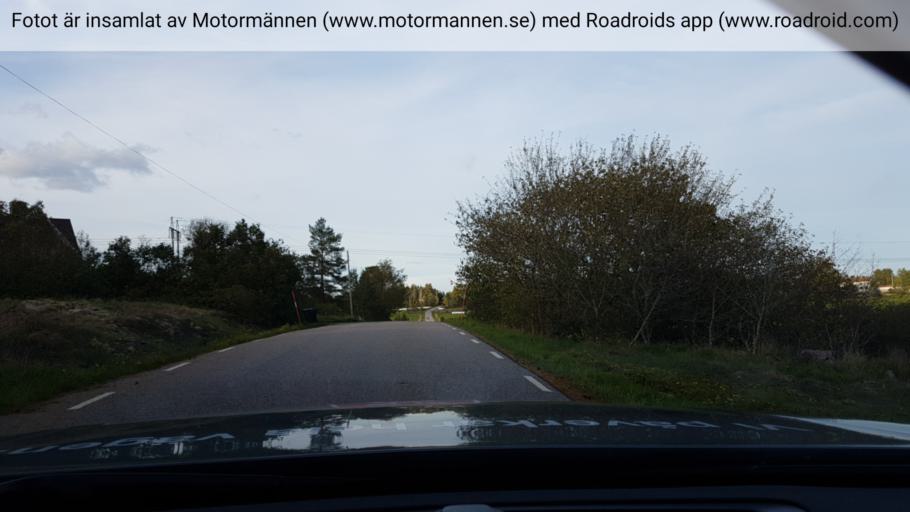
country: SE
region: Kalmar
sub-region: Vasterviks Kommun
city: Forserum
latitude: 57.9314
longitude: 16.4574
